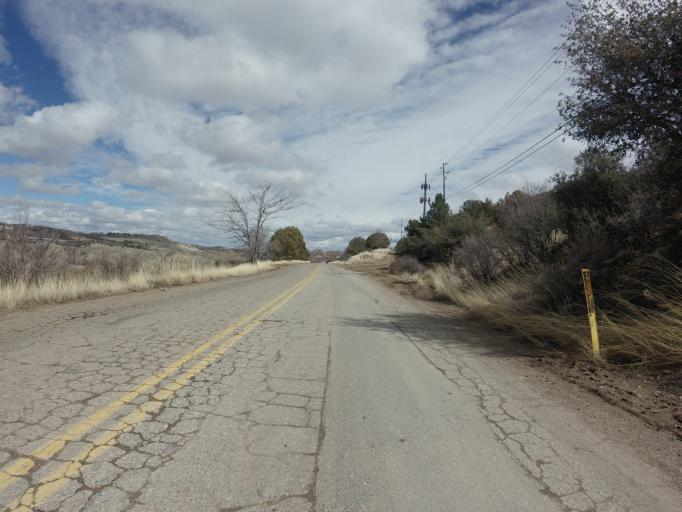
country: US
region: Arizona
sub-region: Yavapai County
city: Prescott
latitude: 34.5667
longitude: -112.4358
